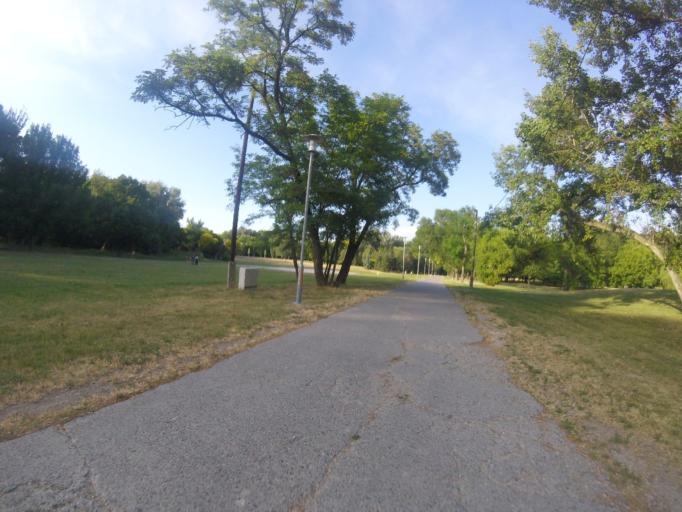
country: HU
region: Budapest
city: Budapest III. keruelet
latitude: 47.5573
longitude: 19.0573
